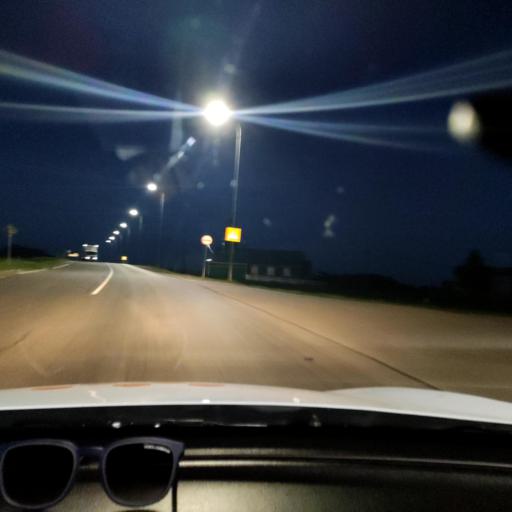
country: RU
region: Tatarstan
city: Rybnaya Sloboda
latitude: 55.4760
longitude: 50.0359
